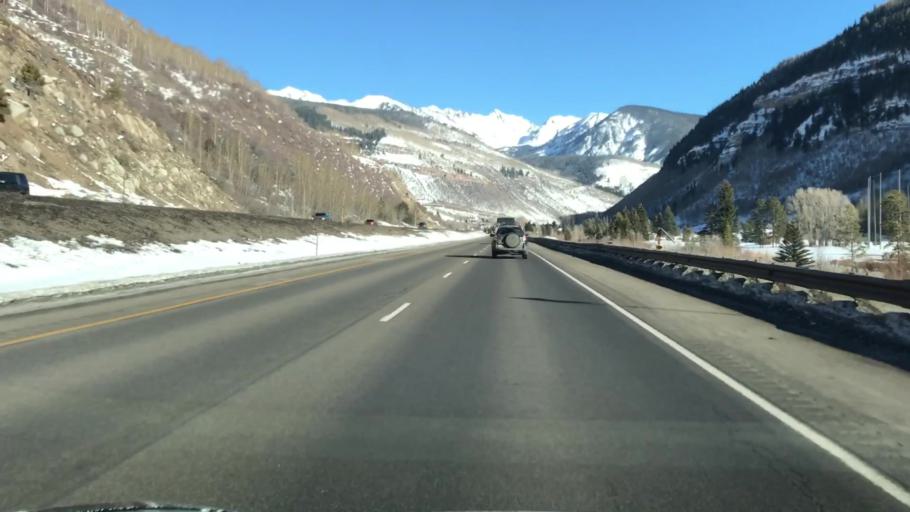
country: US
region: Colorado
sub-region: Eagle County
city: Vail
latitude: 39.6431
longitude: -106.3480
